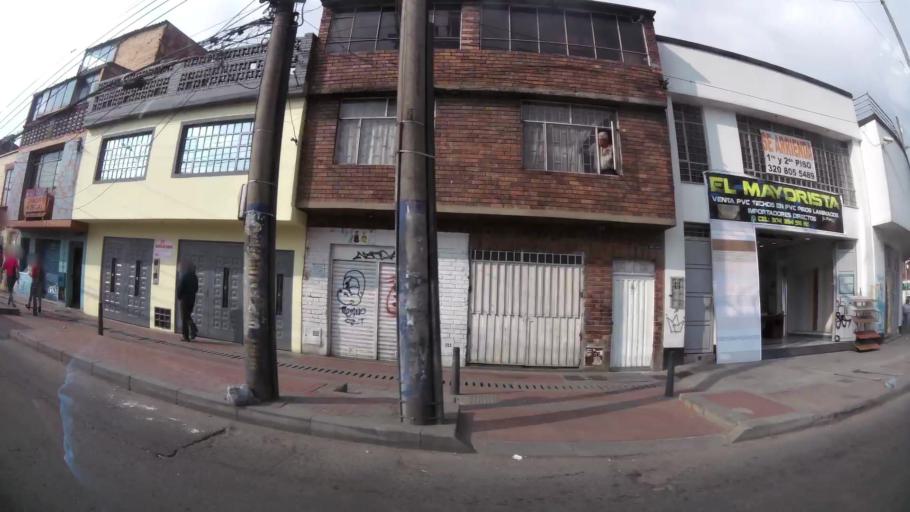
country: CO
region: Bogota D.C.
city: Bogota
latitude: 4.5694
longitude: -74.1258
